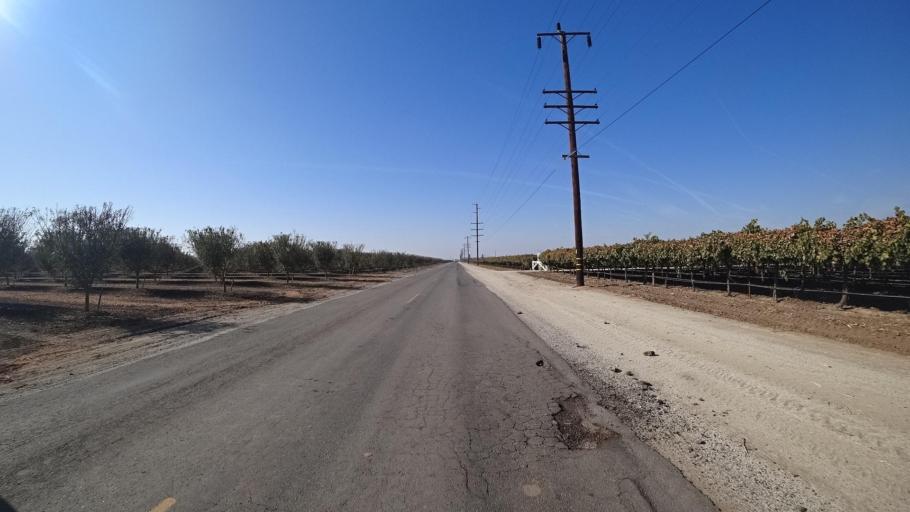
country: US
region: California
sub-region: Kern County
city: McFarland
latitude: 35.7033
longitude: -119.1977
